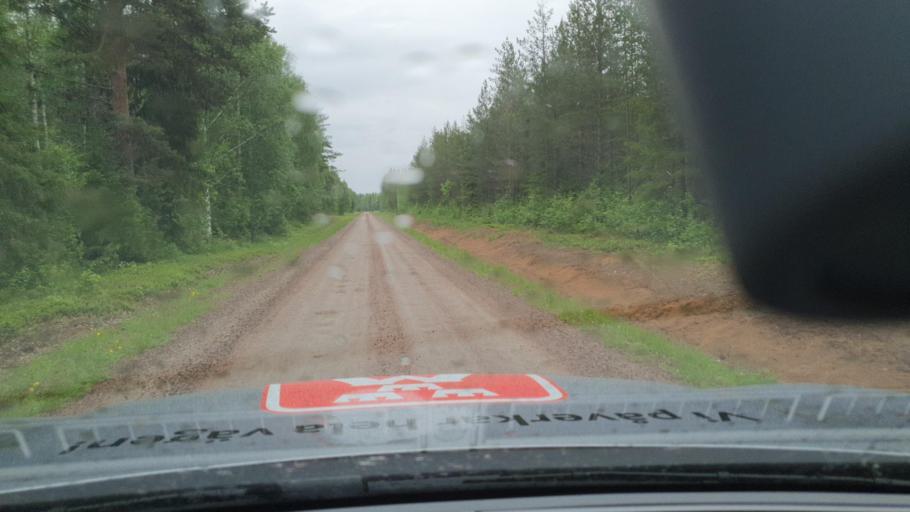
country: SE
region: Norrbotten
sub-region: Overkalix Kommun
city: OEverkalix
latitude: 66.5460
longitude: 22.7445
